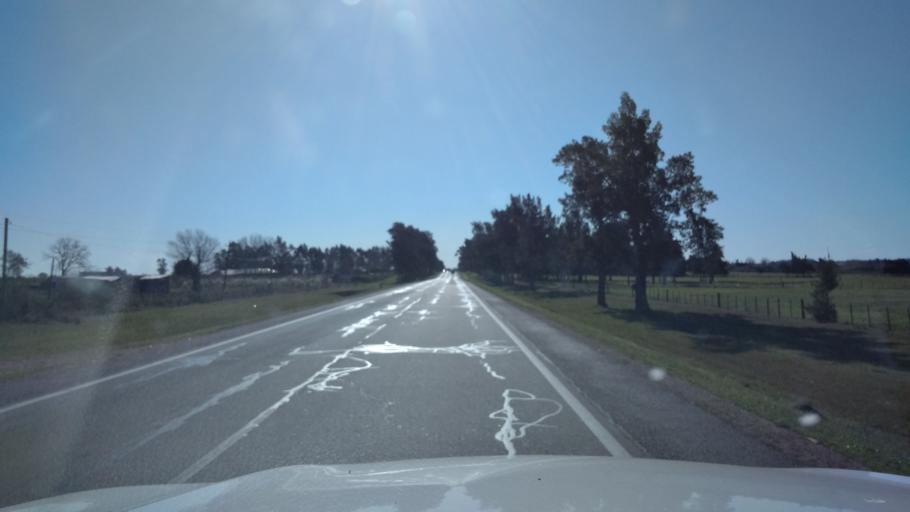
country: UY
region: Canelones
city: San Jacinto
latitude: -34.5814
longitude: -55.8436
